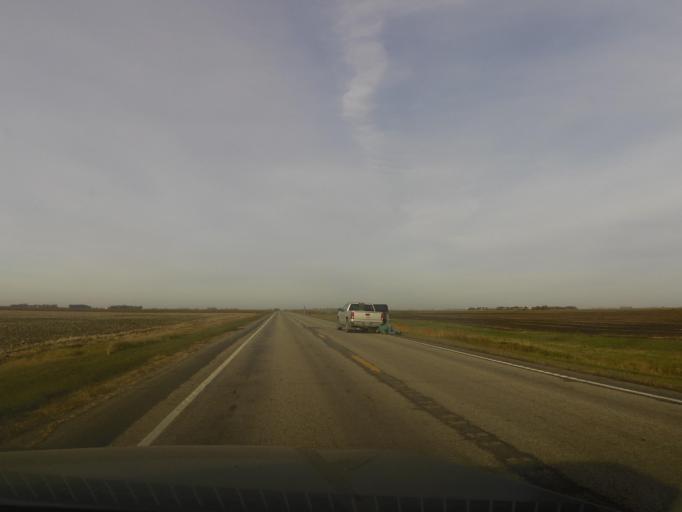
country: US
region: North Dakota
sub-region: Pembina County
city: Cavalier
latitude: 48.8036
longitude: -97.3765
